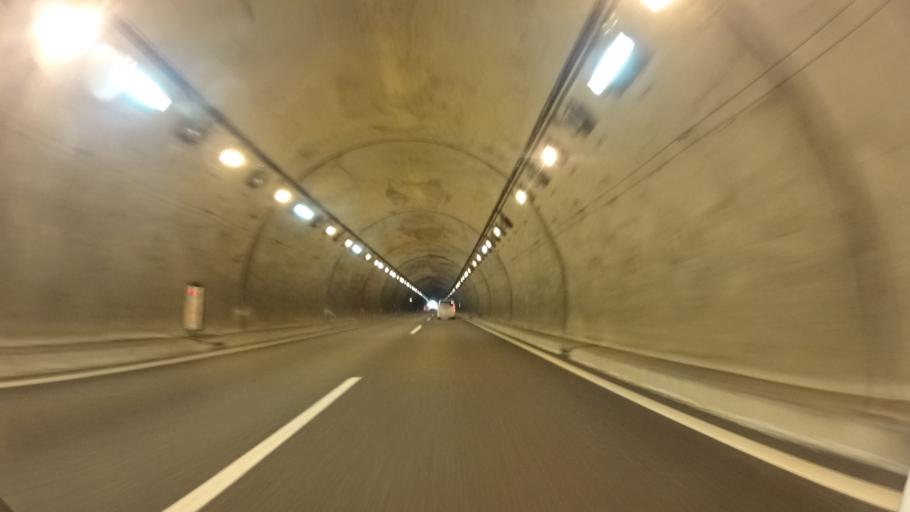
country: JP
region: Ehime
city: Saijo
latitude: 33.8864
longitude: 133.1658
